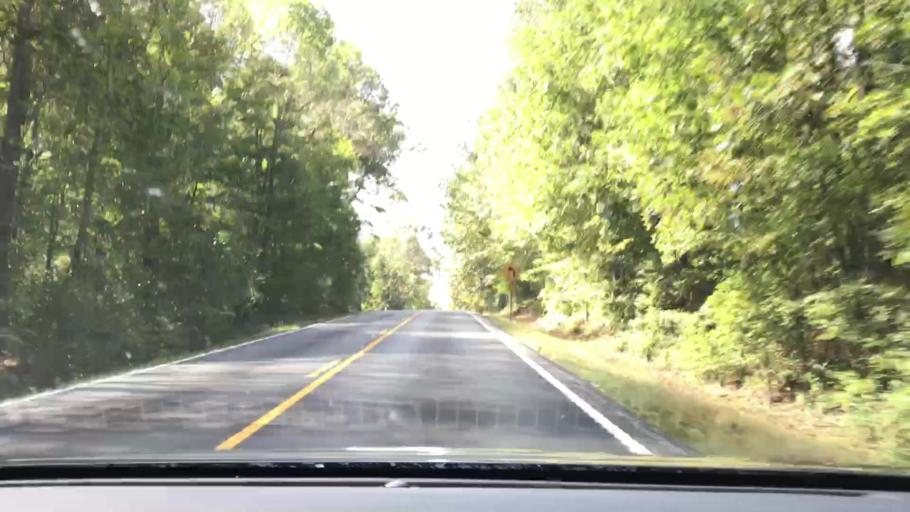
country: US
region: Kentucky
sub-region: Graves County
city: Mayfield
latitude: 36.8720
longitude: -88.5705
